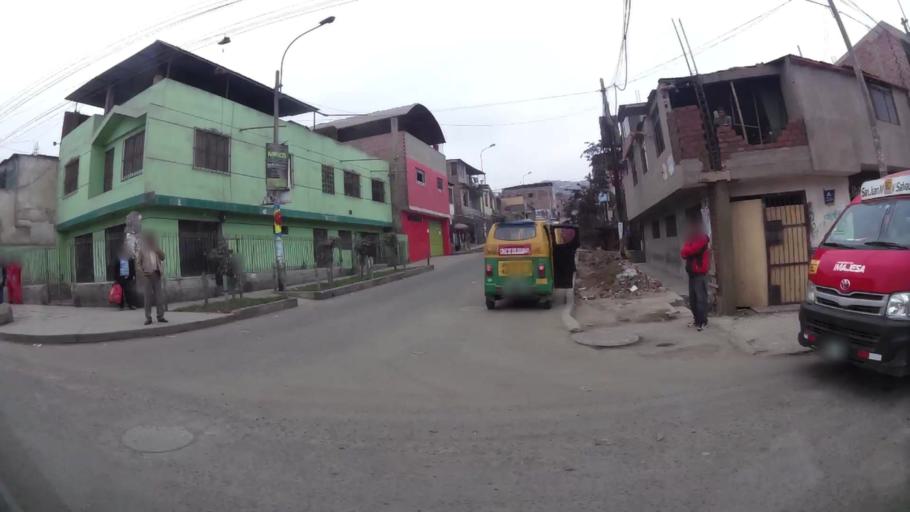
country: PE
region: Lima
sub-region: Lima
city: Surco
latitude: -12.1734
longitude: -76.9624
